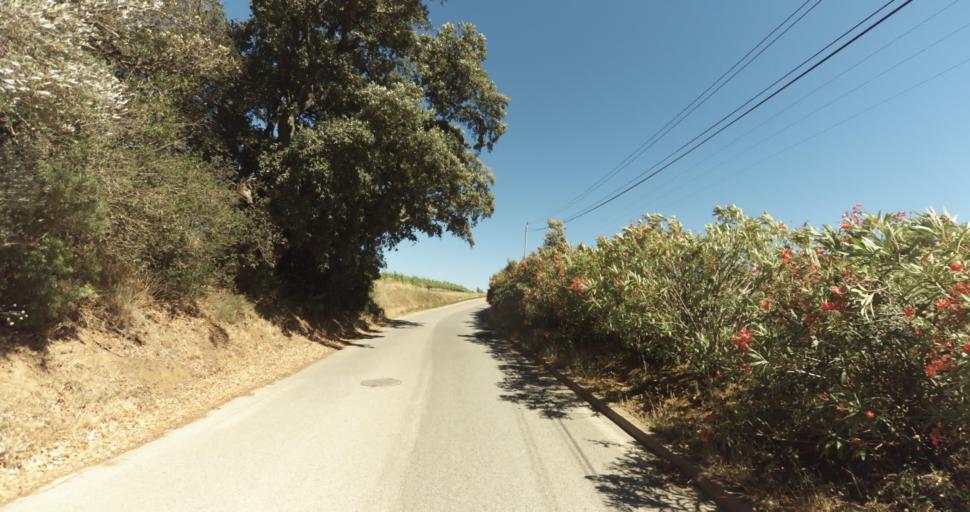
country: FR
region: Provence-Alpes-Cote d'Azur
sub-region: Departement du Var
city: La Croix-Valmer
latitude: 43.2153
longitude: 6.5587
